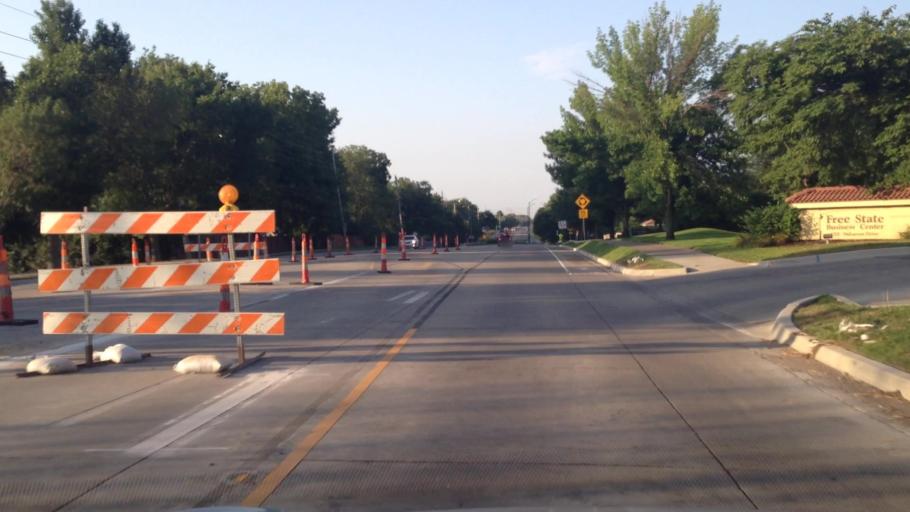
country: US
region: Kansas
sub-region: Douglas County
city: Lawrence
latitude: 38.9648
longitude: -95.3071
